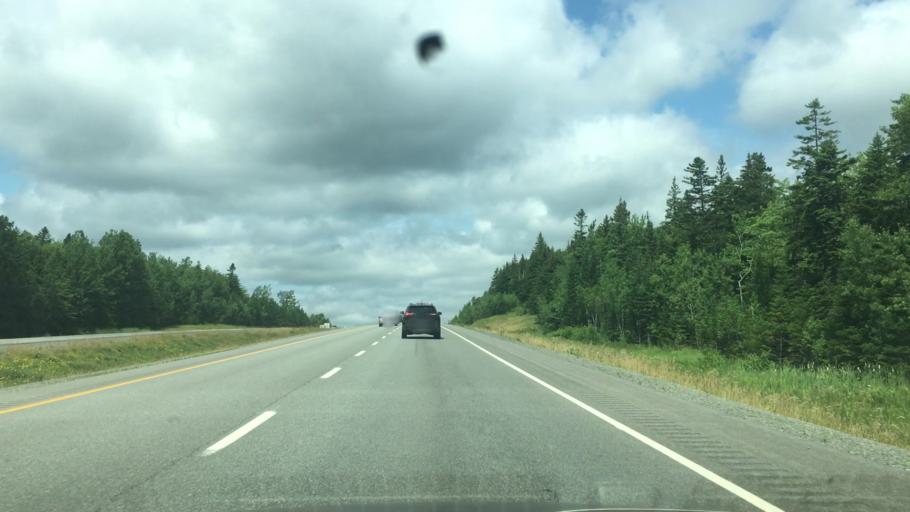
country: CA
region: Nova Scotia
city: Springhill
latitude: 45.7051
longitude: -64.0314
